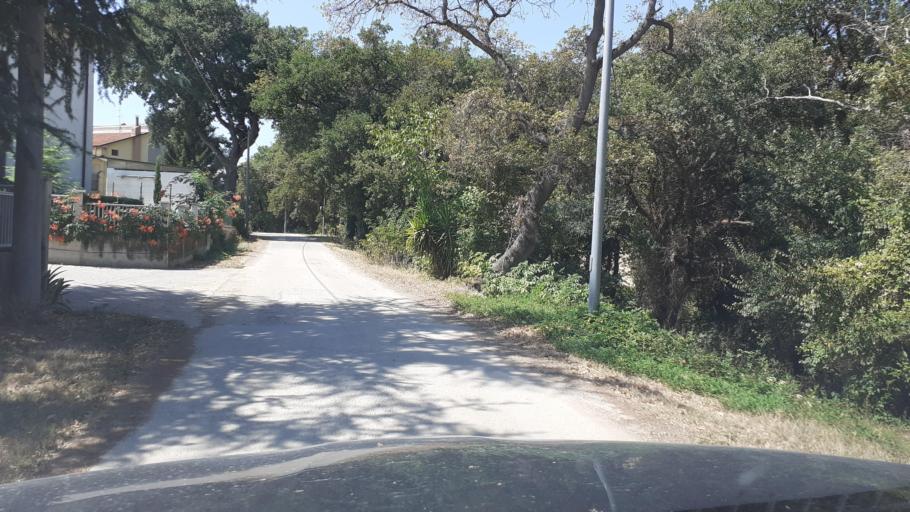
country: IT
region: Abruzzo
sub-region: Provincia di Chieti
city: Santa Maria Imbaro
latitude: 42.2103
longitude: 14.4709
